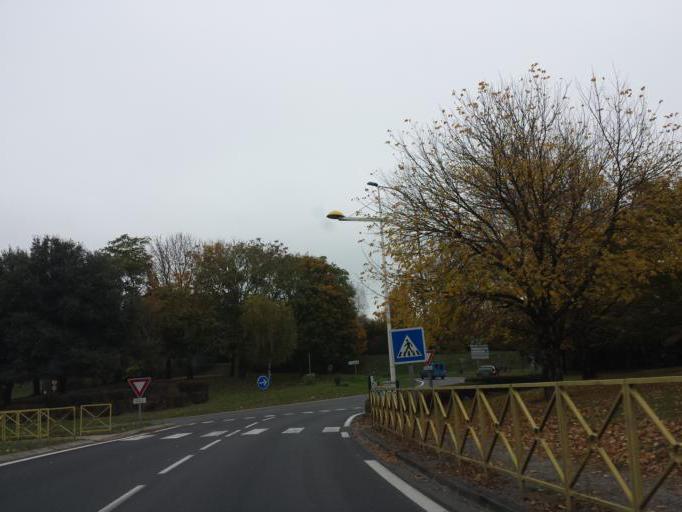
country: FR
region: Poitou-Charentes
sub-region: Departement de la Charente
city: Angouleme
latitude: 45.6290
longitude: 0.1443
